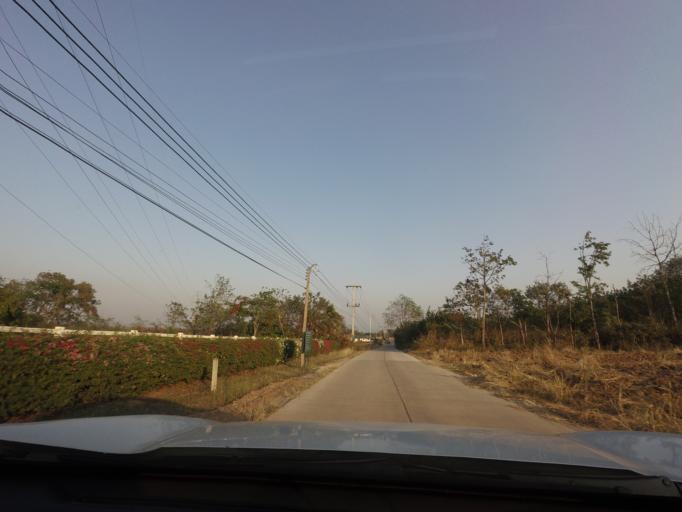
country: TH
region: Nakhon Ratchasima
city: Pak Chong
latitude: 14.6479
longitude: 101.3945
